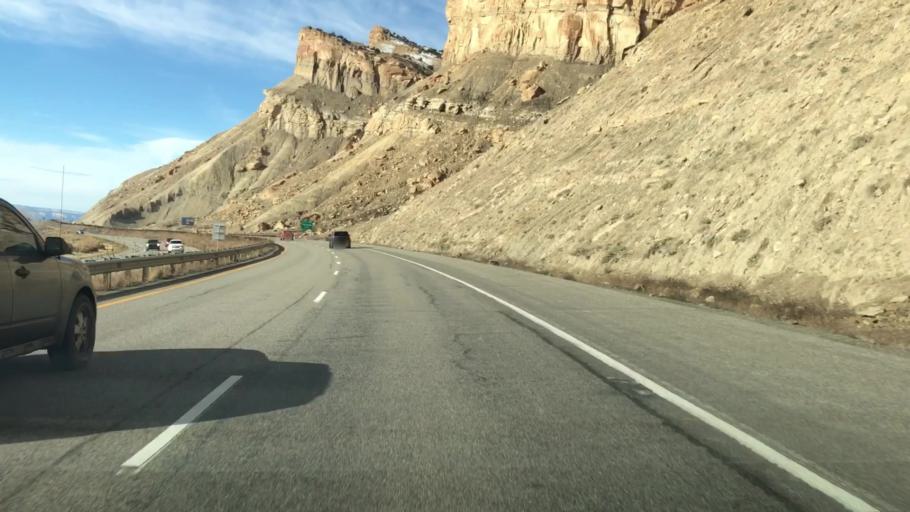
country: US
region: Colorado
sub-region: Mesa County
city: Palisade
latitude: 39.1194
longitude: -108.3378
